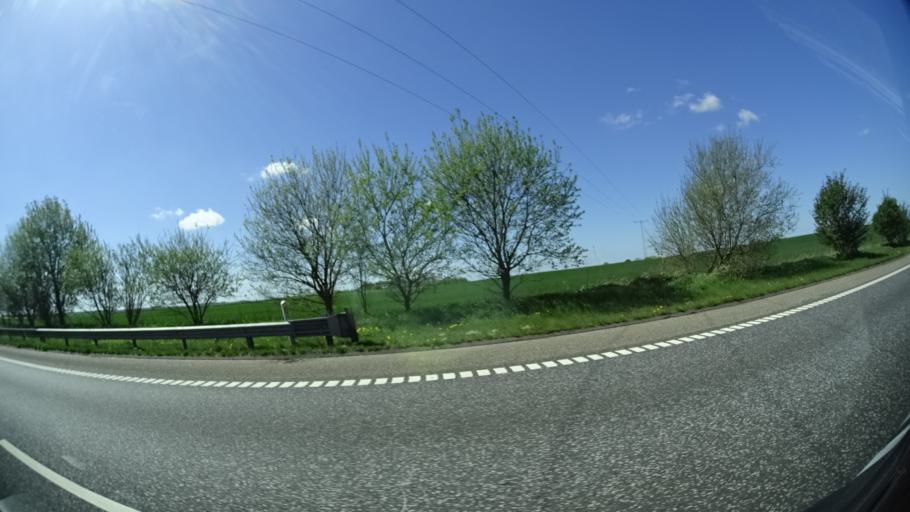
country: DK
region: Central Jutland
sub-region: Favrskov Kommune
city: Hadsten
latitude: 56.3672
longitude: 10.1173
